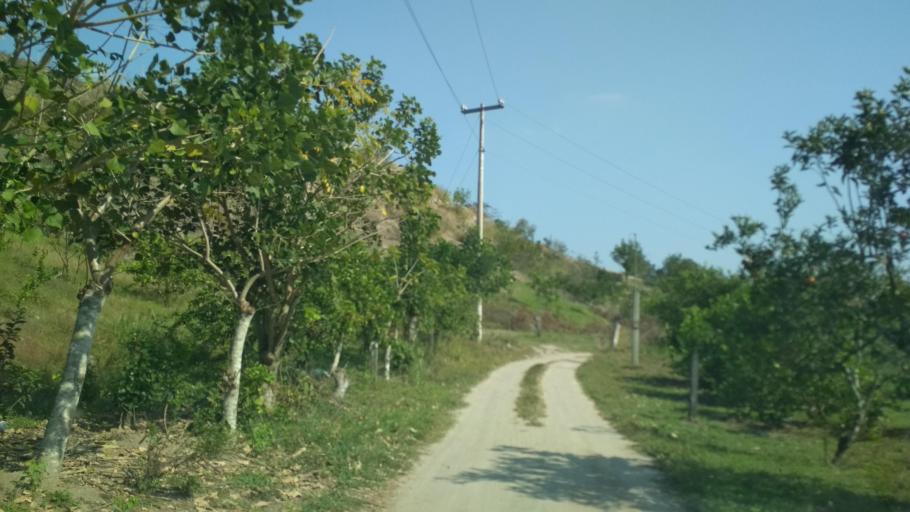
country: MX
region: Puebla
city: San Jose Acateno
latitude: 20.1805
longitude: -97.2578
